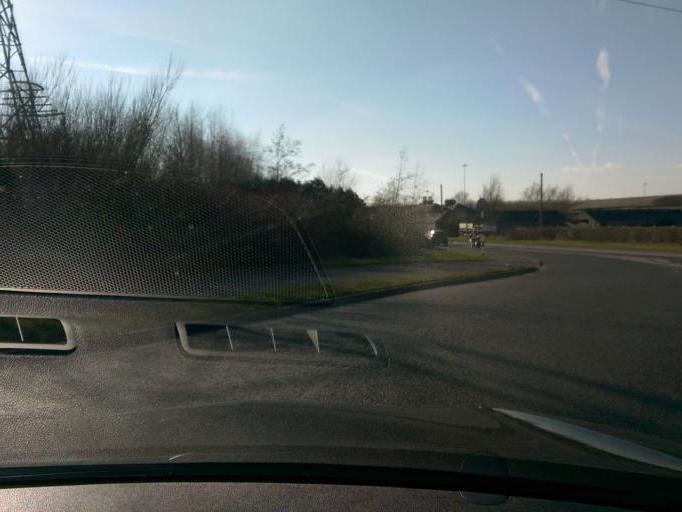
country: IE
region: Leinster
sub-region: Kildare
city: Naas
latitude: 53.2115
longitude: -6.7000
